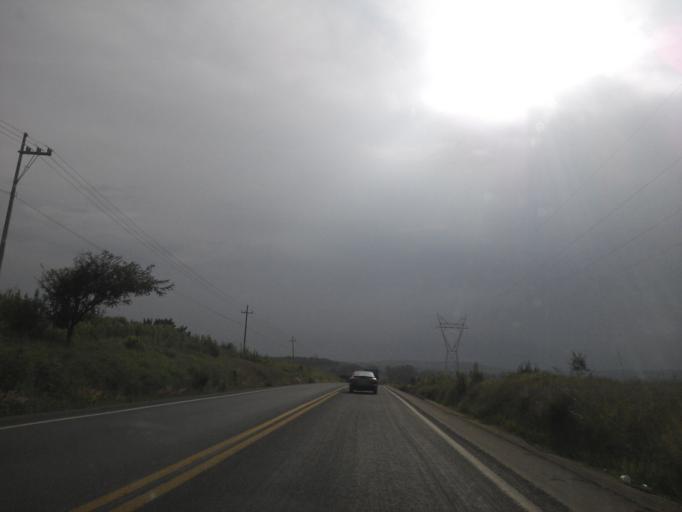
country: MX
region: Jalisco
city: Acatic
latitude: 20.7151
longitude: -102.9312
